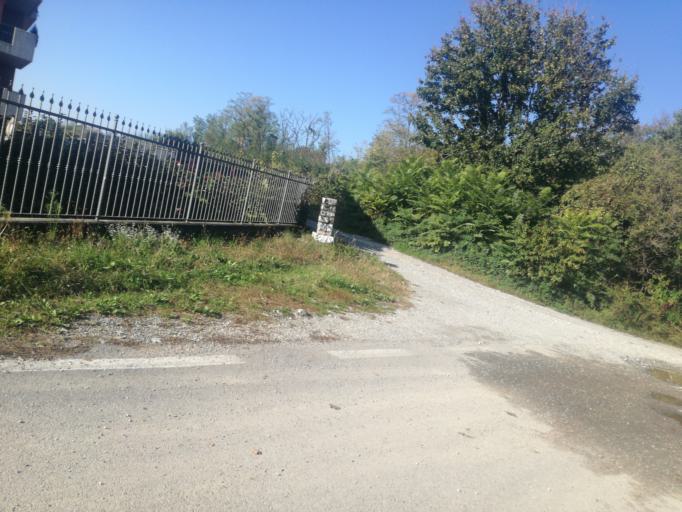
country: IT
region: Lombardy
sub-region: Provincia di Monza e Brianza
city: Porto d'Adda
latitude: 45.6514
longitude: 9.4825
